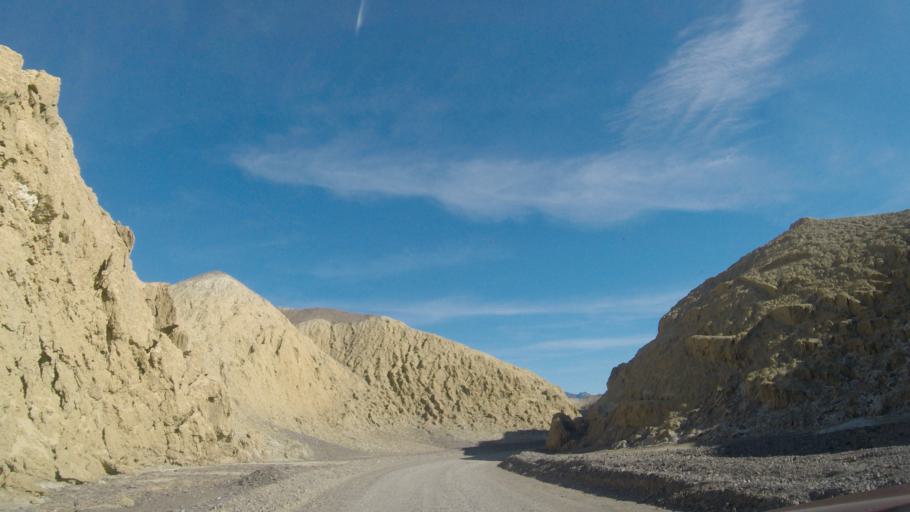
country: US
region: Nevada
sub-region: Nye County
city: Beatty
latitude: 36.4881
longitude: -116.8778
